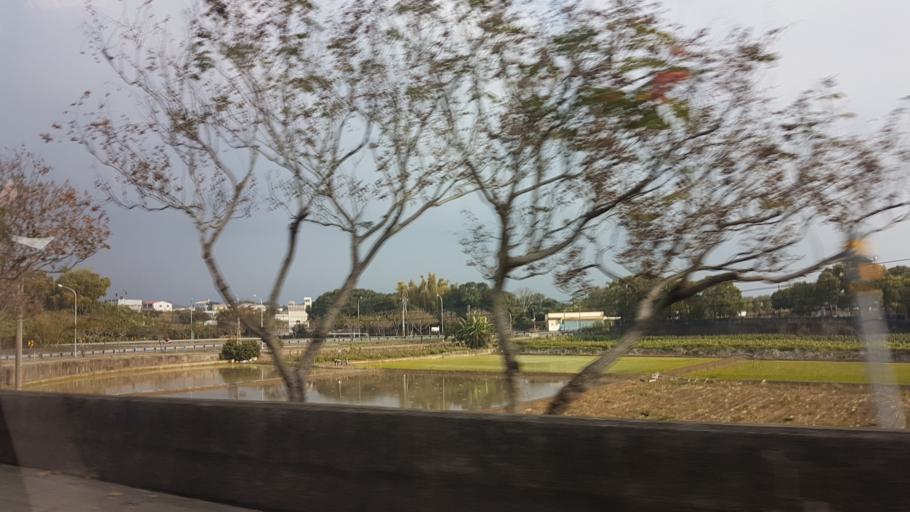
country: TW
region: Taiwan
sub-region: Chiayi
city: Jiayi Shi
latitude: 23.4256
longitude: 120.4307
